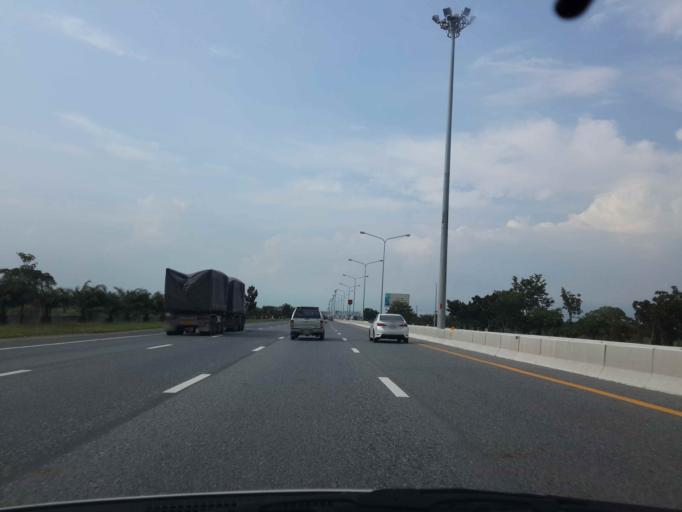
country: TH
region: Chon Buri
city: Phan Thong
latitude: 13.4722
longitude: 101.0459
